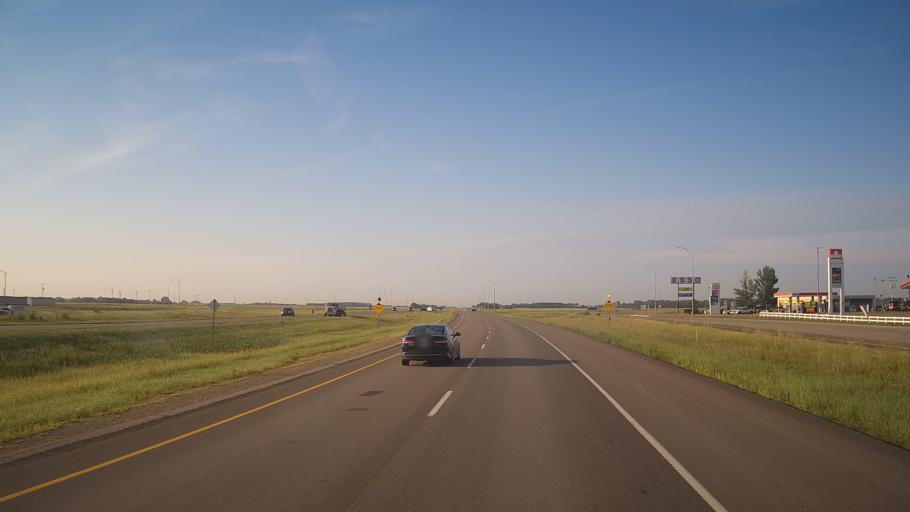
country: CA
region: Saskatchewan
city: Saskatoon
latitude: 52.0579
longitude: -106.6001
